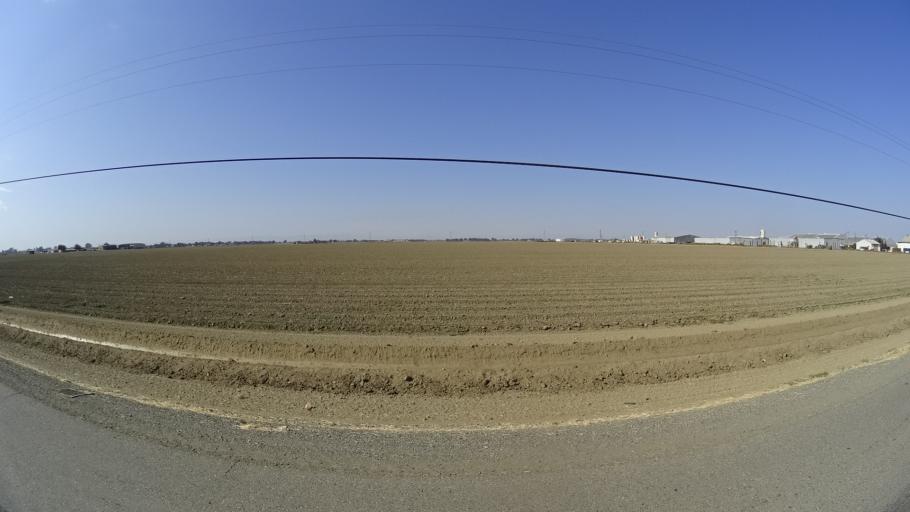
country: US
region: California
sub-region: Yolo County
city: Woodland
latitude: 38.7467
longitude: -121.7292
